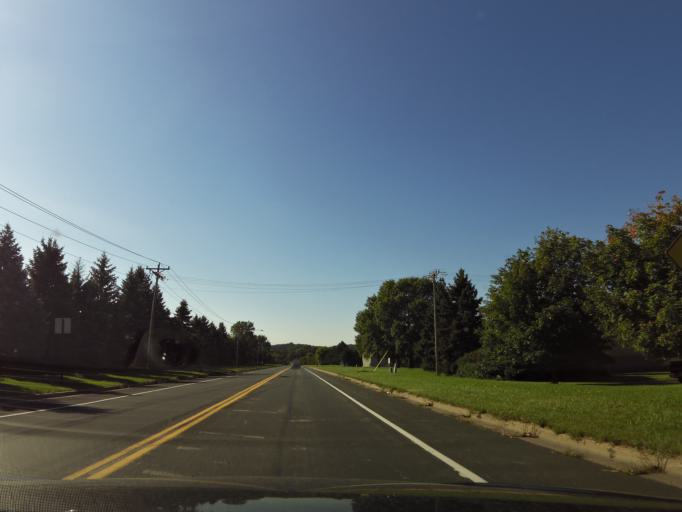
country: US
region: Minnesota
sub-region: Scott County
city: Savage
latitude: 44.7415
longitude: -93.3236
